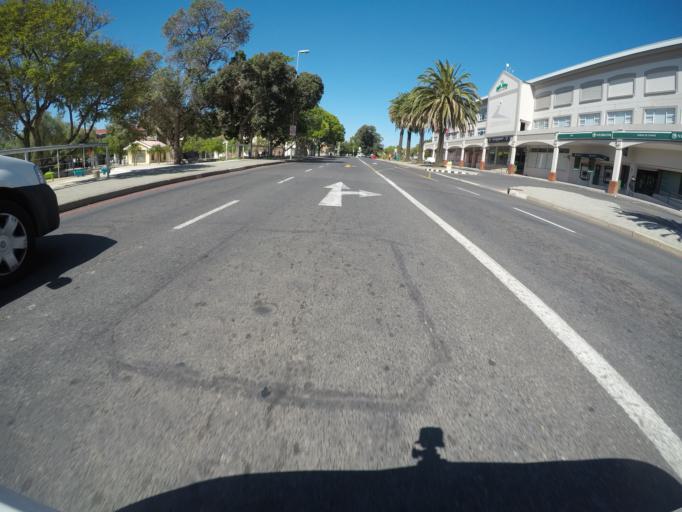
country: ZA
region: Western Cape
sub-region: City of Cape Town
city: Kraaifontein
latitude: -33.8329
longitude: 18.6475
